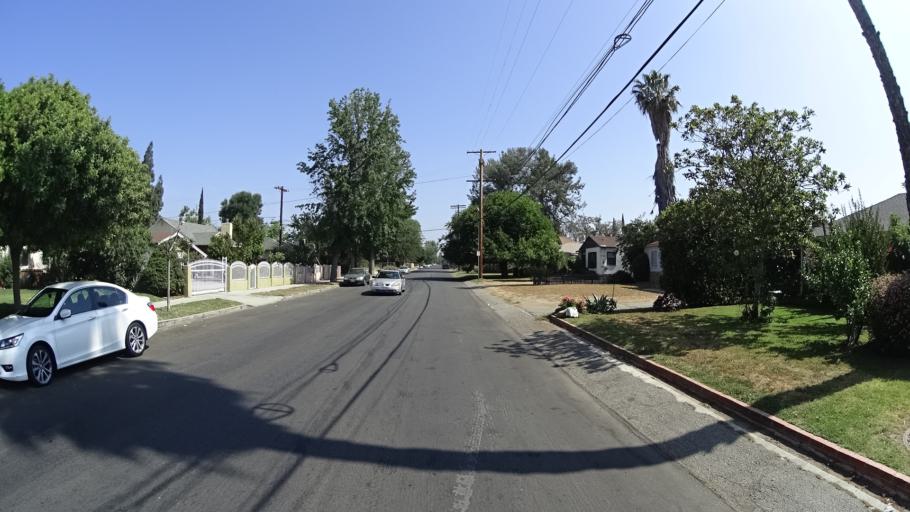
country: US
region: California
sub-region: Los Angeles County
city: Van Nuys
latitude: 34.1948
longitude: -118.4531
